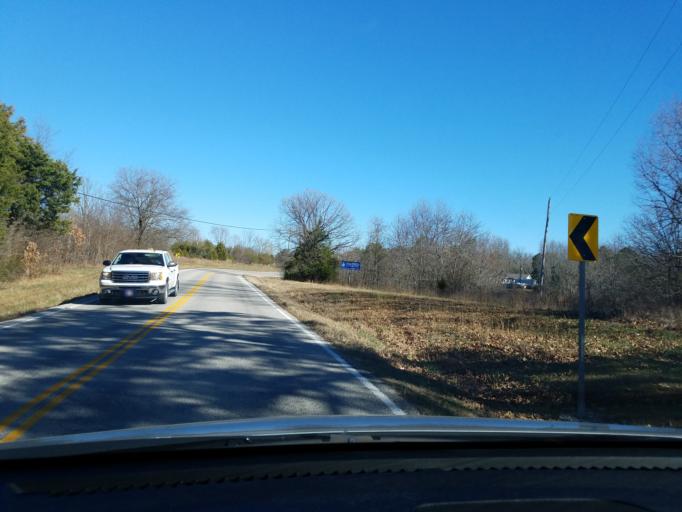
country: US
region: Missouri
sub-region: Stone County
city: Kimberling City
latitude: 36.5438
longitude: -93.3484
